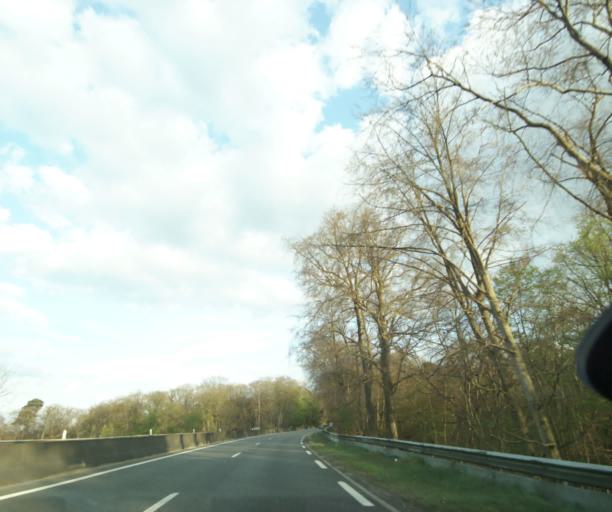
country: FR
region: Ile-de-France
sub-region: Departement de Seine-et-Marne
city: Barbizon
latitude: 48.4412
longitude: 2.6501
